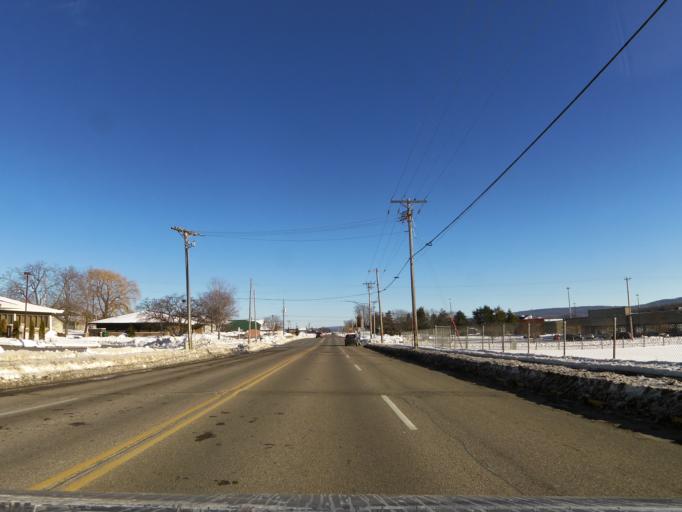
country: US
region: Wisconsin
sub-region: Sauk County
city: Baraboo
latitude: 43.4747
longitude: -89.7226
